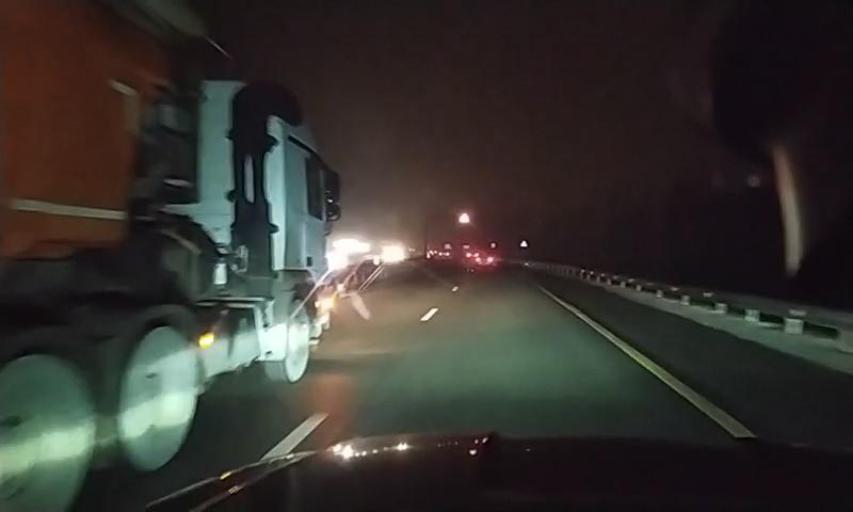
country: RU
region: Leningrad
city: Agalatovo
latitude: 60.2039
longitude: 30.3605
